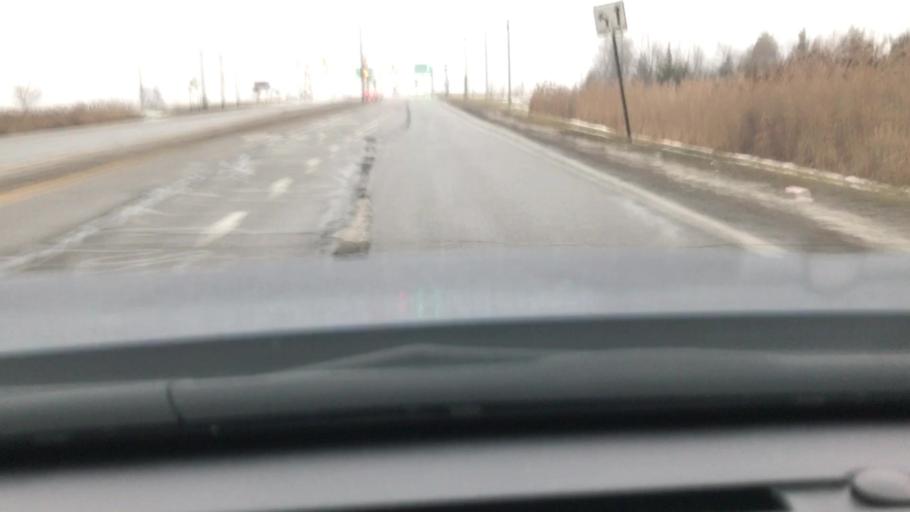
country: US
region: Michigan
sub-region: Oakland County
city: Wixom
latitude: 42.4971
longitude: -83.5160
